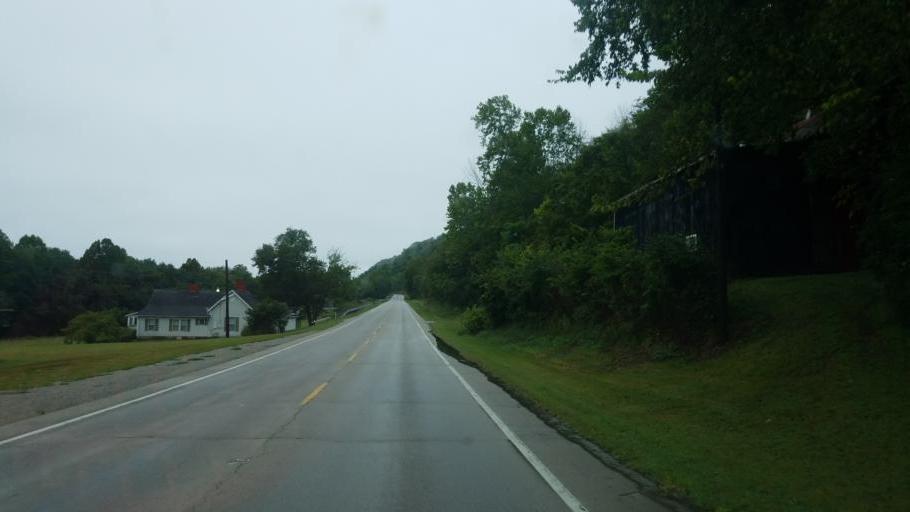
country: US
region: Kentucky
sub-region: Mason County
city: Maysville
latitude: 38.6467
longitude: -83.7135
